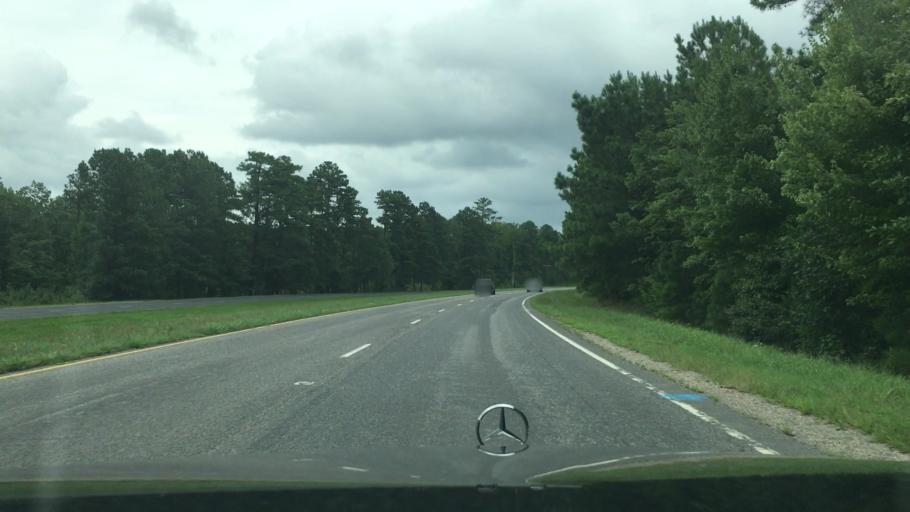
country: US
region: Virginia
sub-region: Chesterfield County
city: Woodlake
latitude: 37.3894
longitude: -77.7497
